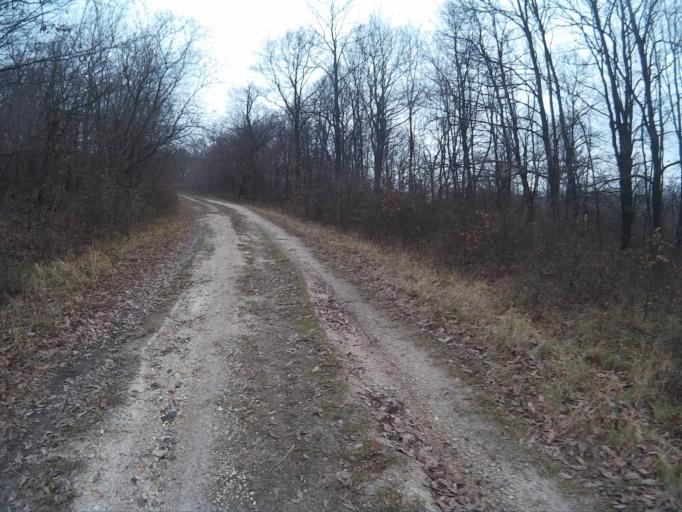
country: HU
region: Veszprem
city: Tapolca
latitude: 46.9706
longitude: 17.4898
